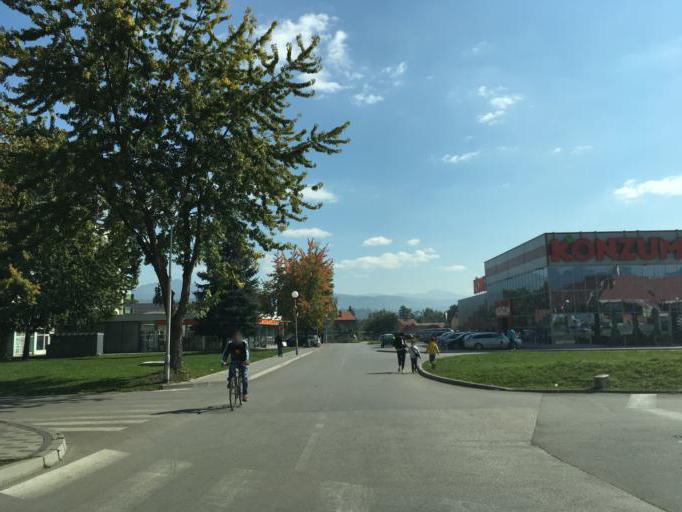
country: BA
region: Federation of Bosnia and Herzegovina
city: Bugojno
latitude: 44.0520
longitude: 17.4479
